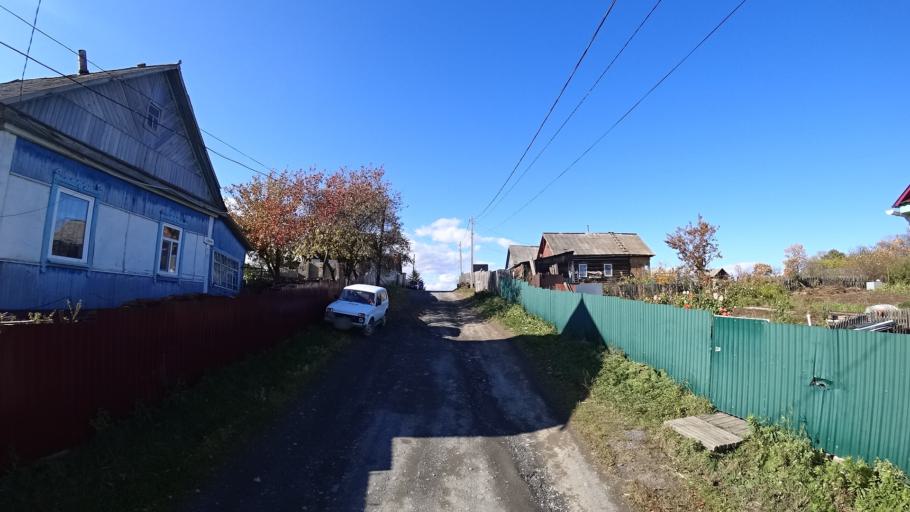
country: RU
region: Khabarovsk Krai
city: Amursk
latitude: 50.2313
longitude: 136.9177
